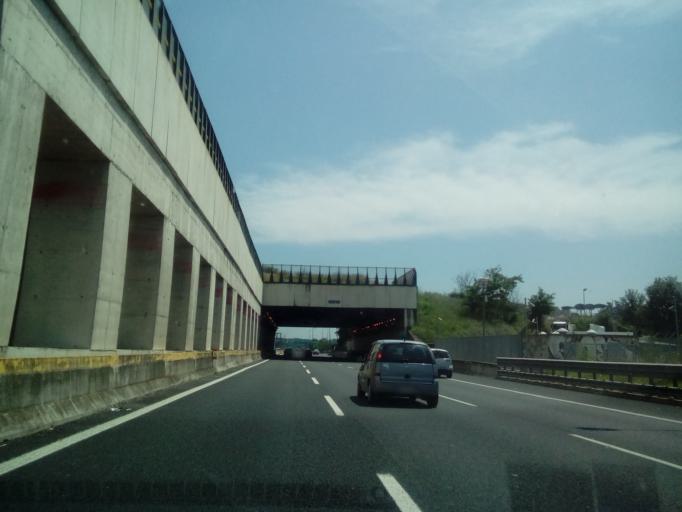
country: IT
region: Latium
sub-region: Citta metropolitana di Roma Capitale
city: La Massimina-Casal Lumbroso
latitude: 41.8933
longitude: 12.3813
